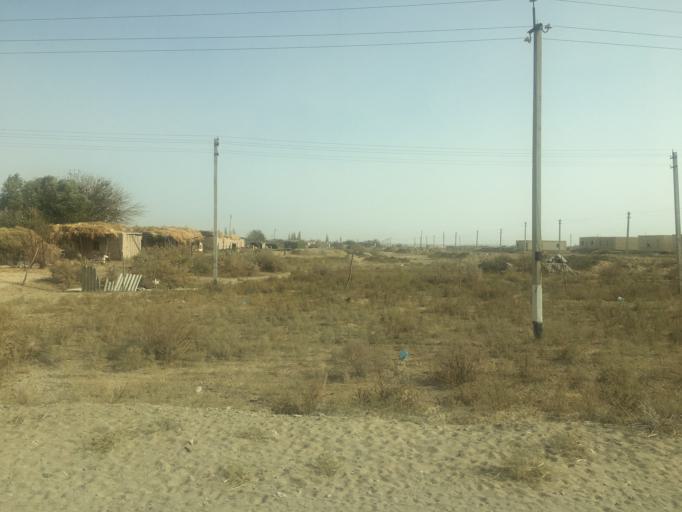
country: TM
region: Lebap
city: Gazojak
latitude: 41.1627
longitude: 61.3980
